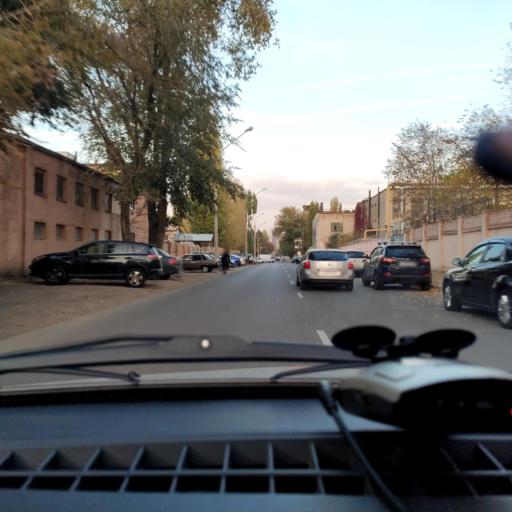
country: RU
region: Voronezj
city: Voronezh
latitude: 51.6611
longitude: 39.1580
